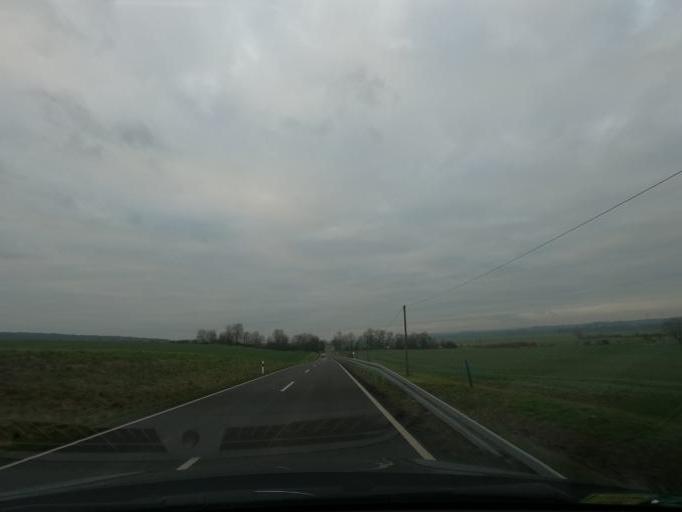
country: DE
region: Lower Saxony
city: Hedeper
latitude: 52.0386
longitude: 10.7093
